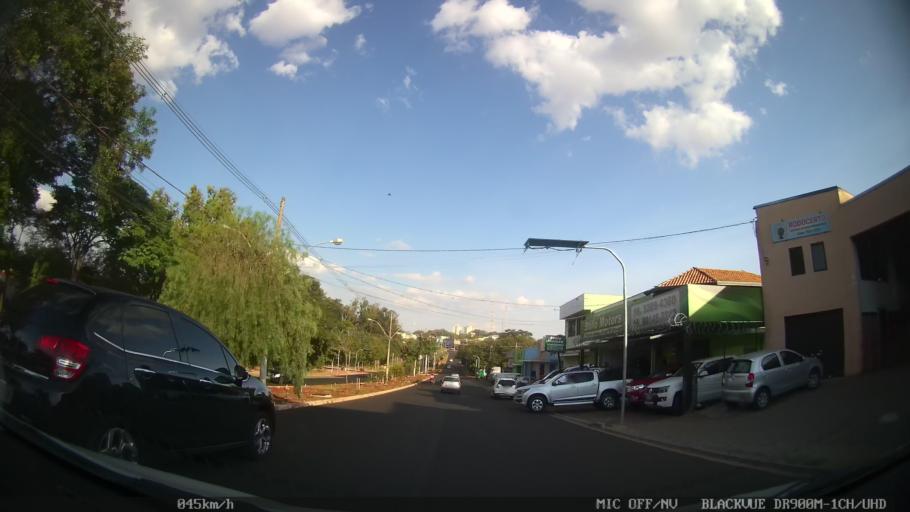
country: BR
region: Sao Paulo
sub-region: Ribeirao Preto
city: Ribeirao Preto
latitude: -21.1434
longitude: -47.8326
